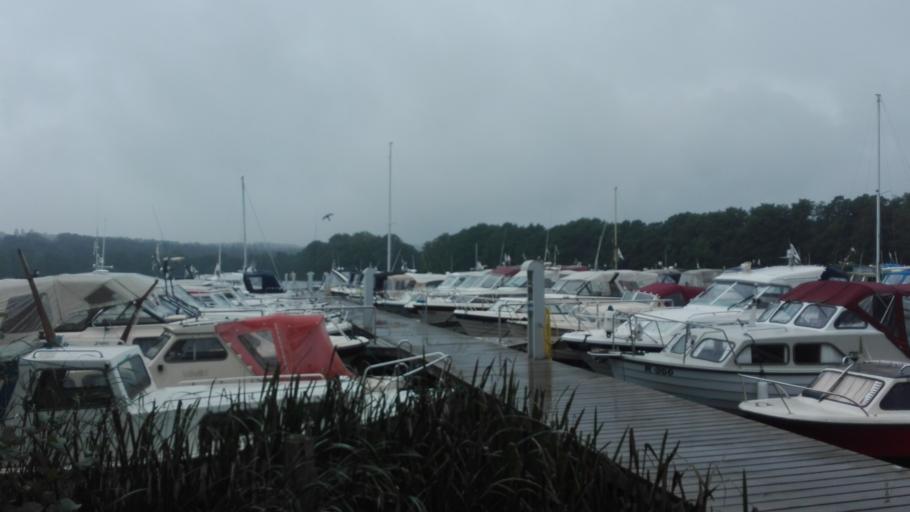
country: DK
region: Central Jutland
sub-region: Skanderborg Kommune
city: Ry
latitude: 56.0950
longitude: 9.7518
